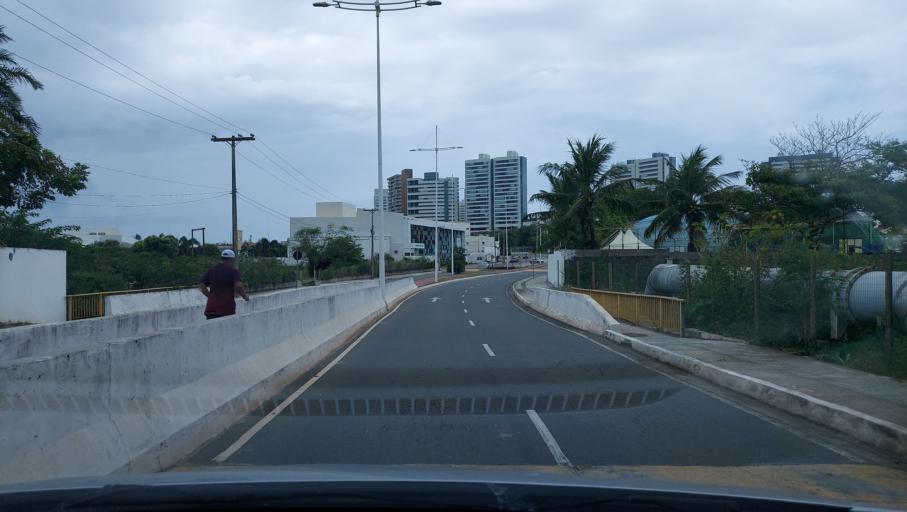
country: BR
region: Bahia
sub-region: Lauro De Freitas
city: Lauro de Freitas
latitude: -12.9564
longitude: -38.3995
